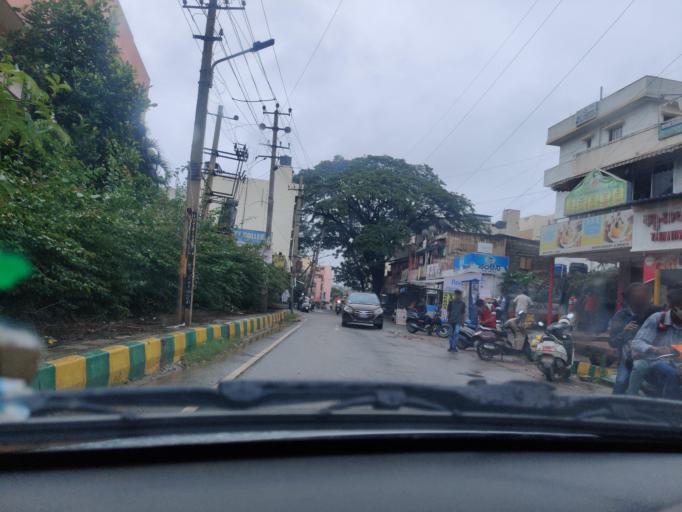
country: IN
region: Karnataka
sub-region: Bangalore Urban
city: Bangalore
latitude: 13.0280
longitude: 77.6396
